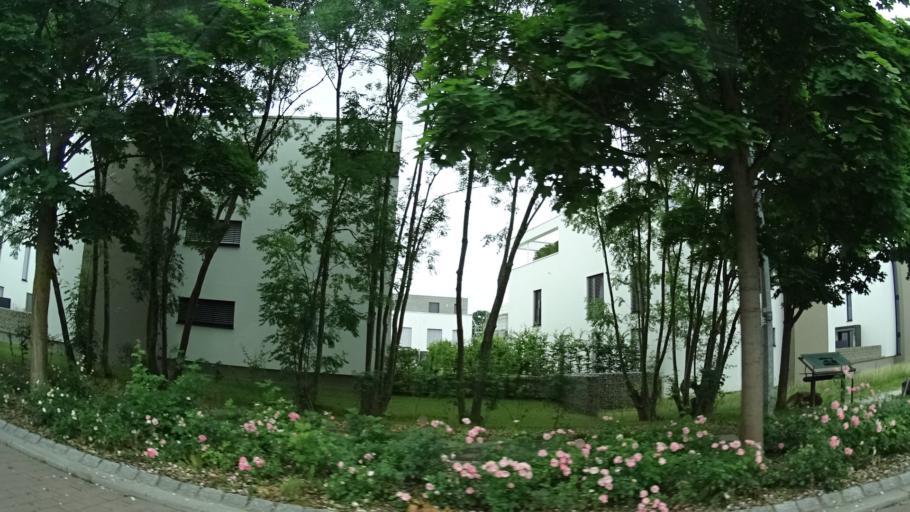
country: LU
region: Luxembourg
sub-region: Canton d'Esch-sur-Alzette
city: Bettembourg
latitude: 49.5123
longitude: 6.1123
